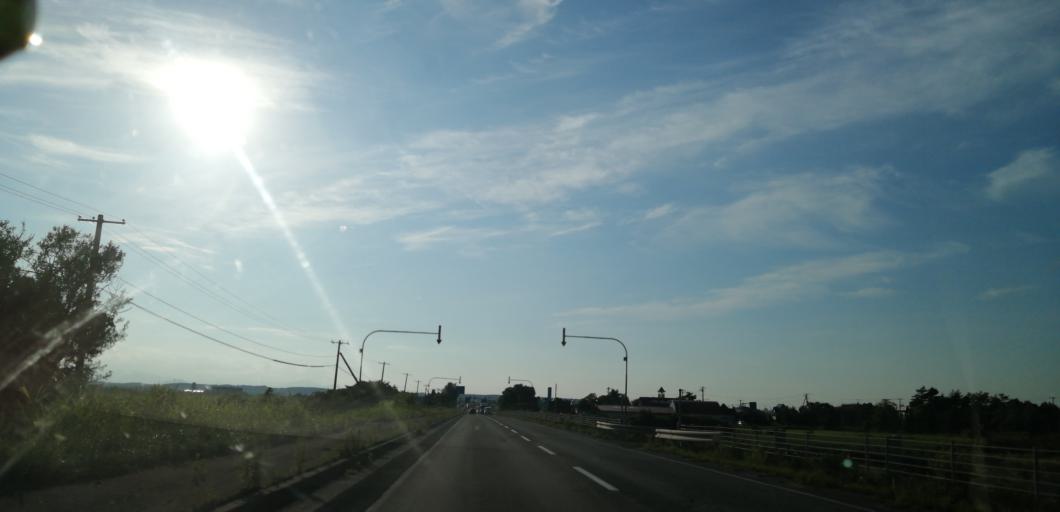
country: JP
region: Hokkaido
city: Kitahiroshima
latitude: 42.9951
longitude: 141.5942
